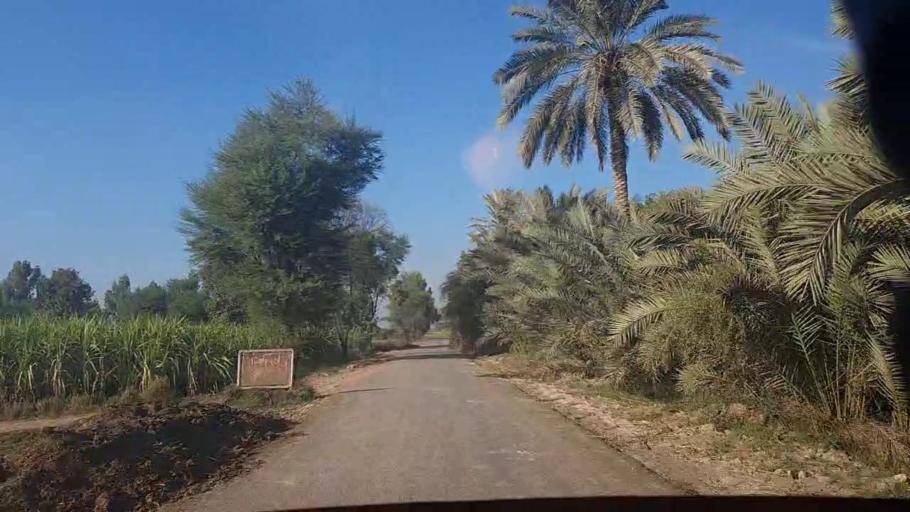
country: PK
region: Sindh
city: Sobhadero
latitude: 27.3884
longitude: 68.4190
